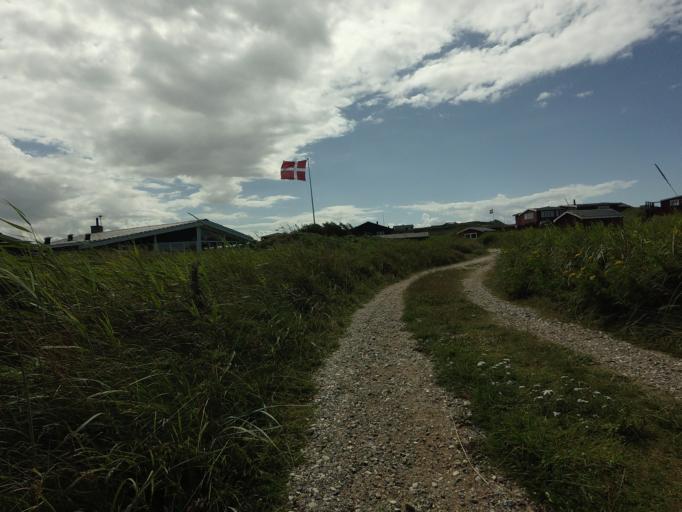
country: DK
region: North Denmark
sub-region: Jammerbugt Kommune
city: Pandrup
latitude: 57.3556
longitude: 9.6946
